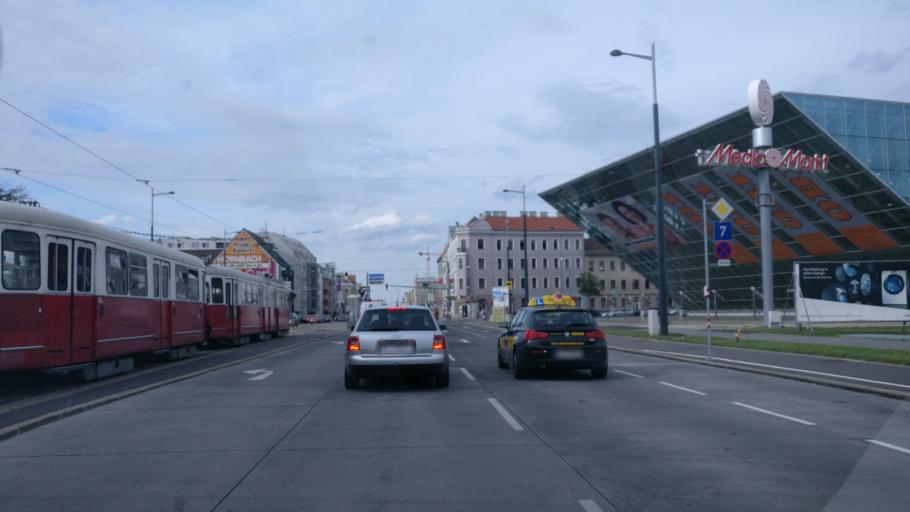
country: AT
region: Lower Austria
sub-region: Politischer Bezirk Korneuburg
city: Langenzersdorf
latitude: 48.2705
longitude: 16.4053
